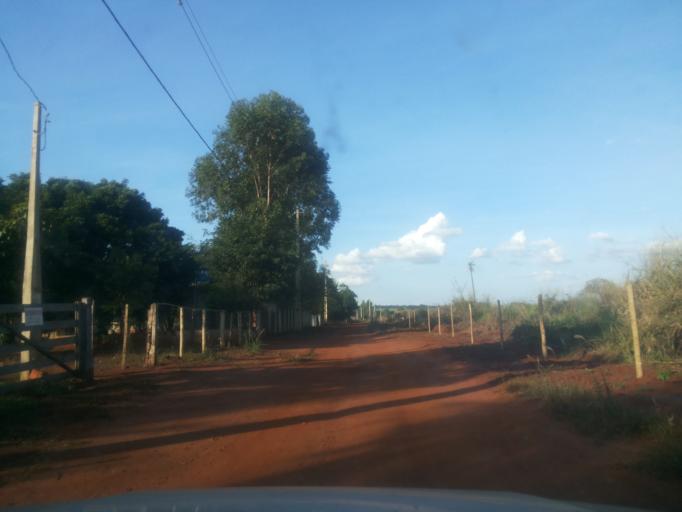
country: BR
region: Minas Gerais
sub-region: Santa Vitoria
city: Santa Vitoria
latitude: -18.9852
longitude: -50.3686
